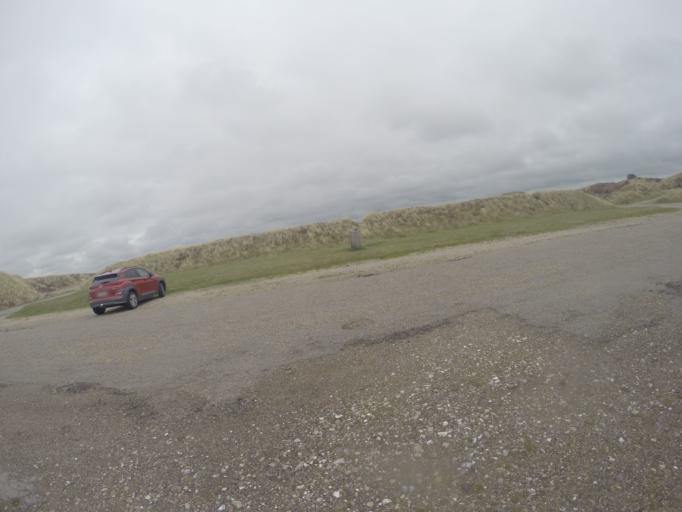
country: DK
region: North Denmark
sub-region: Thisted Kommune
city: Hurup
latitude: 56.9283
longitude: 8.3393
